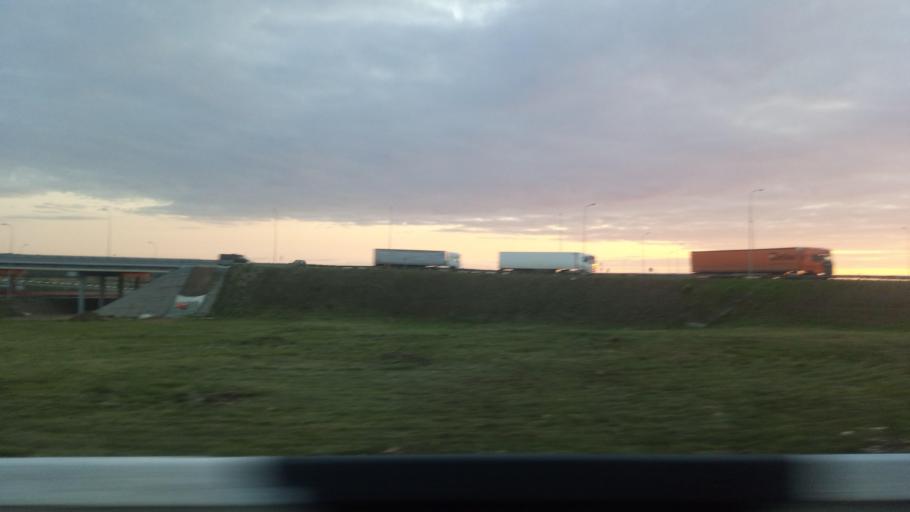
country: RU
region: Chelyabinsk
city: Poletayevo
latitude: 55.0054
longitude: 61.1617
